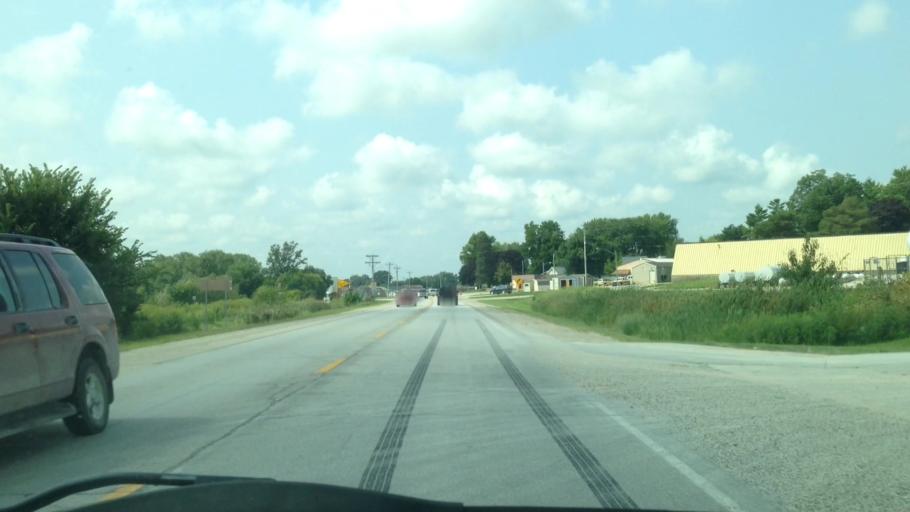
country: US
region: Iowa
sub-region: Benton County
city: Walford
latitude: 41.8810
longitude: -91.8299
